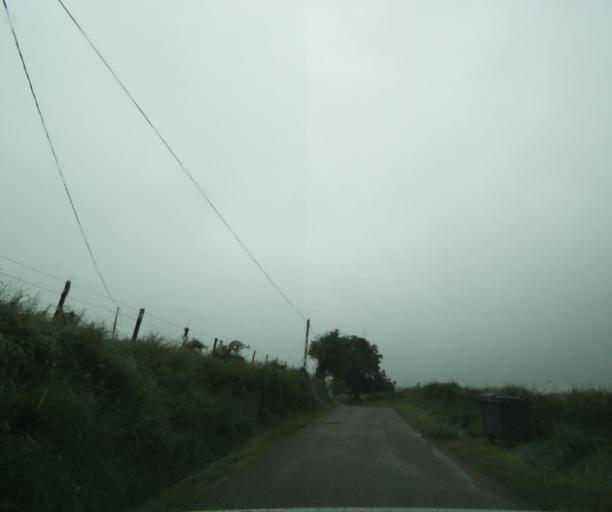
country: FR
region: Bourgogne
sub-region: Departement de Saone-et-Loire
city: Charolles
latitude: 46.4146
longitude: 4.3827
